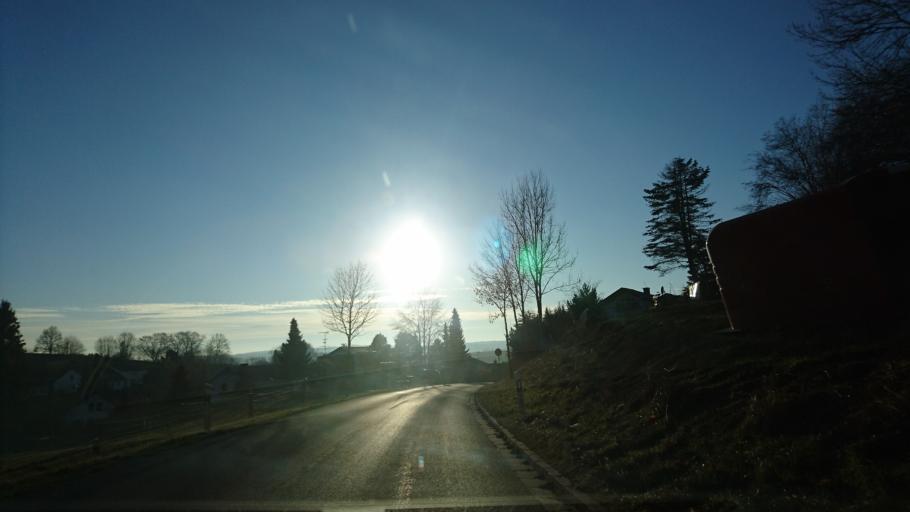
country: DE
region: Bavaria
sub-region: Swabia
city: Horgau
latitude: 48.4144
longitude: 10.6855
